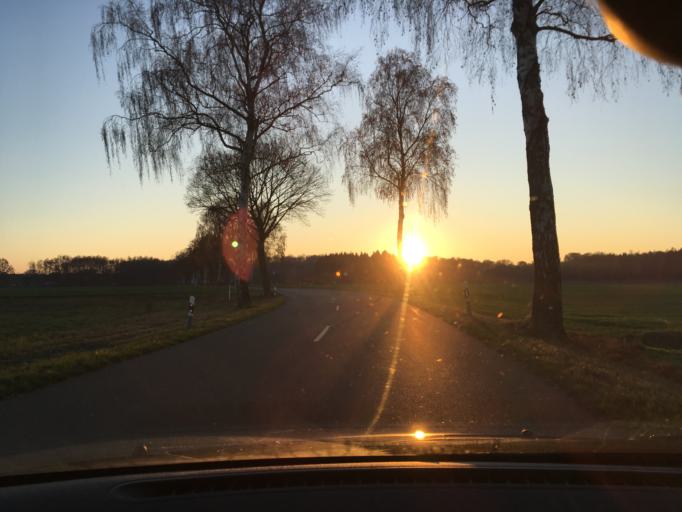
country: DE
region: Lower Saxony
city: Ebstorf
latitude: 53.0407
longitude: 10.4282
